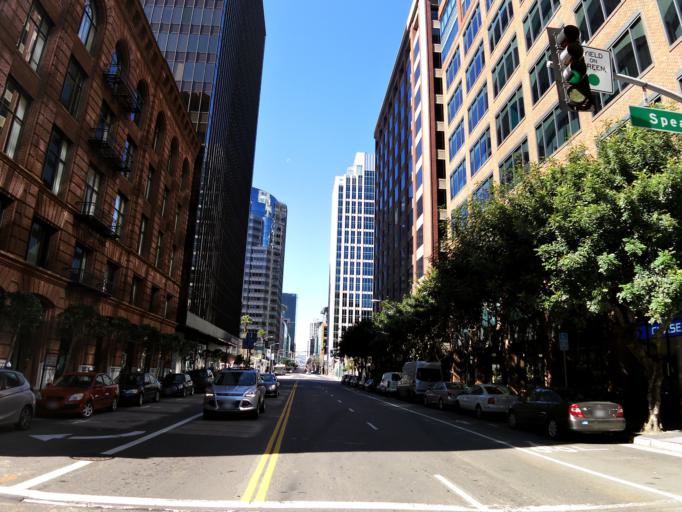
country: US
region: California
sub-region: San Francisco County
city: San Francisco
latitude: 37.7914
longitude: -122.3926
